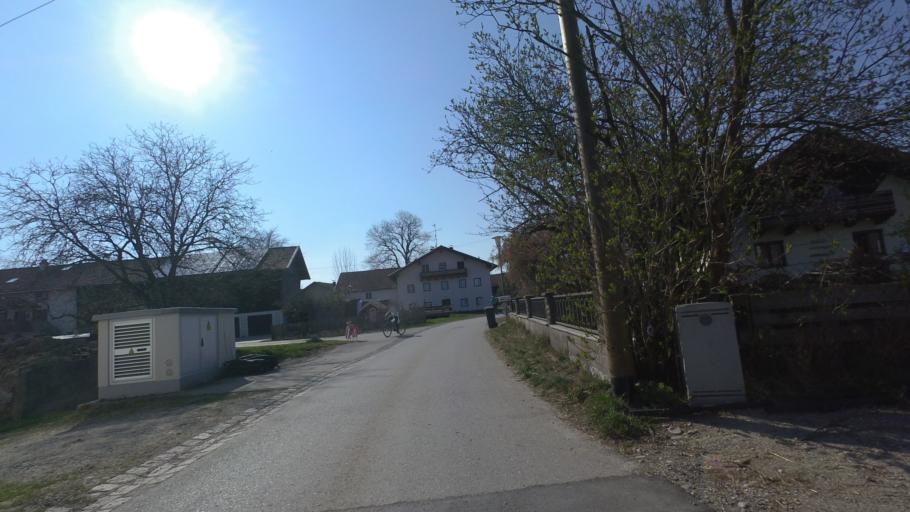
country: DE
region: Bavaria
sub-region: Upper Bavaria
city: Traunreut
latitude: 47.9457
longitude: 12.5979
